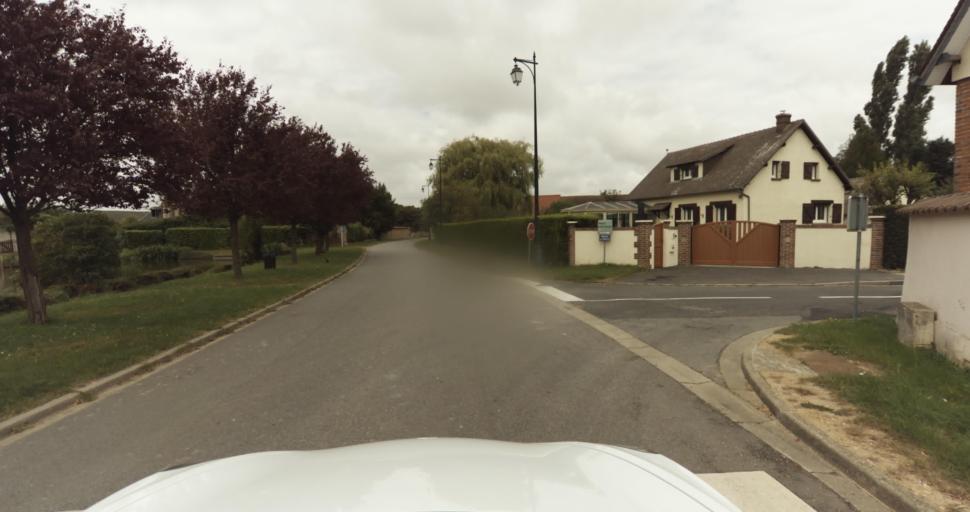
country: FR
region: Haute-Normandie
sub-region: Departement de l'Eure
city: Claville
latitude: 49.0256
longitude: 1.0340
